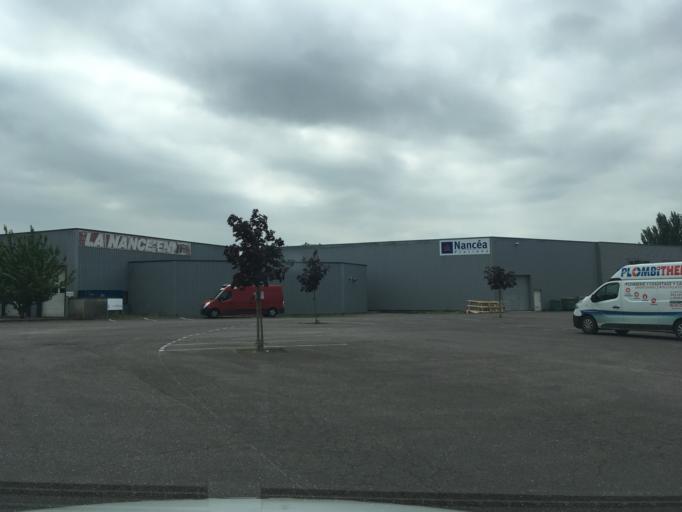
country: FR
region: Lorraine
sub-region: Departement de Meurthe-et-Moselle
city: Tomblaine
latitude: 48.6852
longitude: 6.2048
